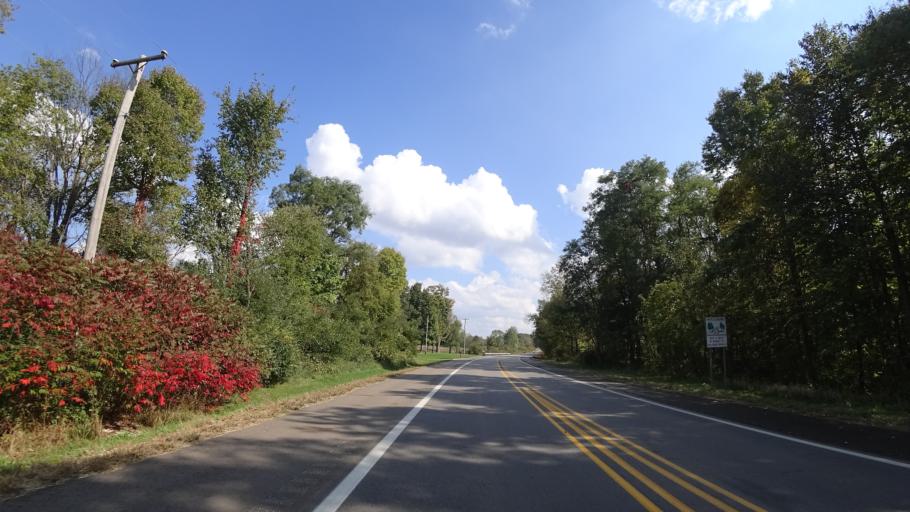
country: US
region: Michigan
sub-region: Calhoun County
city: Athens
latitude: 42.0608
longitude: -85.2324
